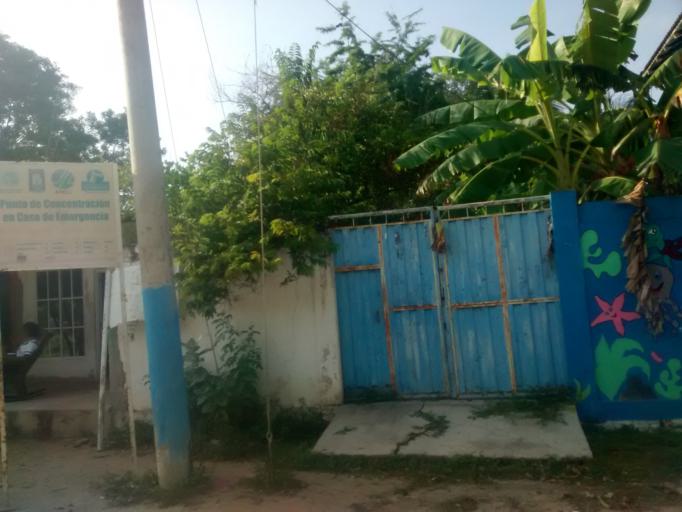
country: CO
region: Bolivar
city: Turbana
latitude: 10.1415
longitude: -75.6862
